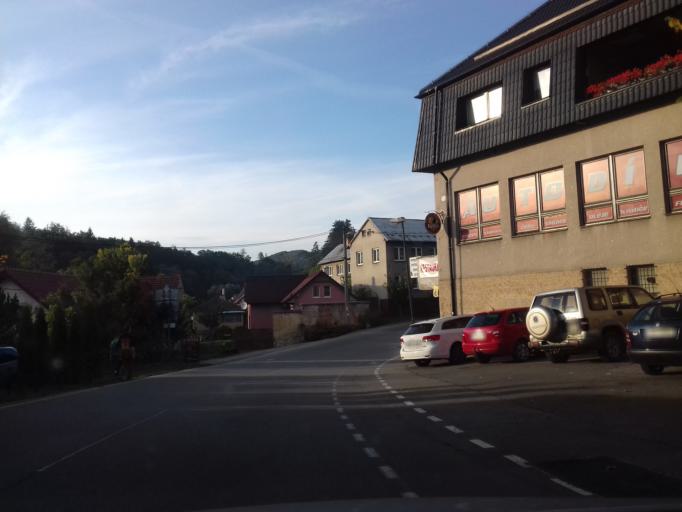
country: CZ
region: Central Bohemia
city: Kamenny Privoz
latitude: 49.8625
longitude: 14.5038
